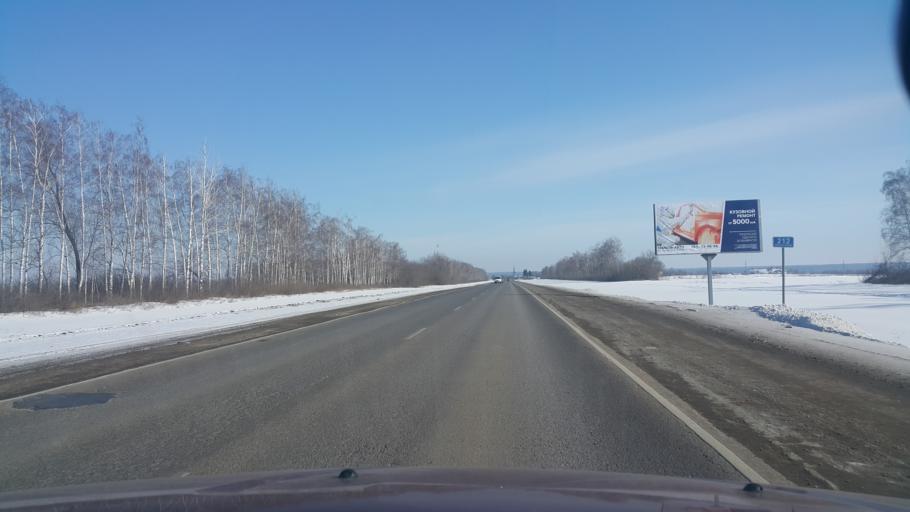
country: RU
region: Tambov
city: Pokrovo-Prigorodnoye
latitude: 52.6656
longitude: 41.3910
